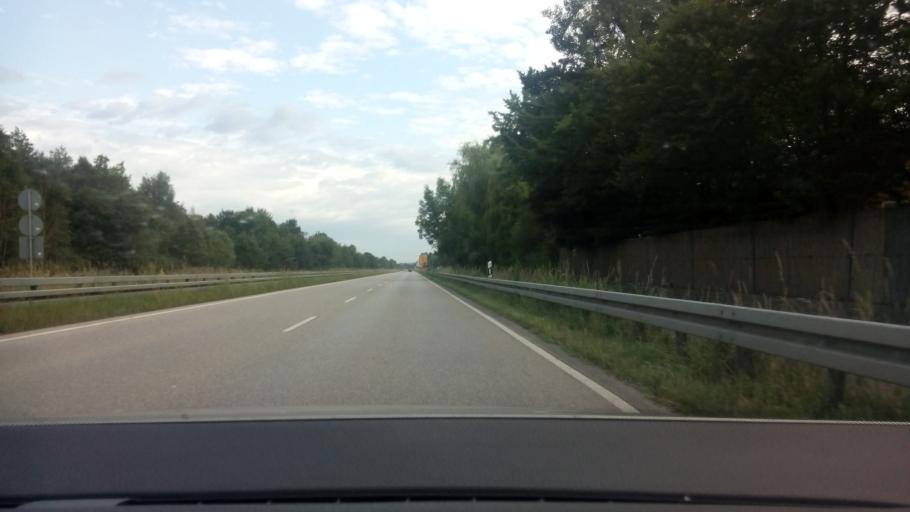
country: DE
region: Bavaria
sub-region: Upper Bavaria
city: Unterschleissheim
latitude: 48.2589
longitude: 11.5980
